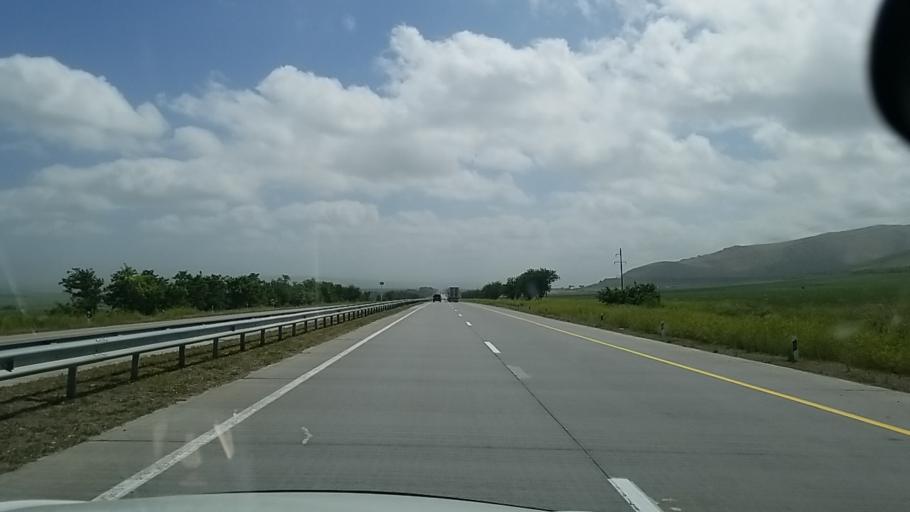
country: KZ
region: Ongtustik Qazaqstan
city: Sastobe
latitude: 42.5459
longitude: 70.0732
